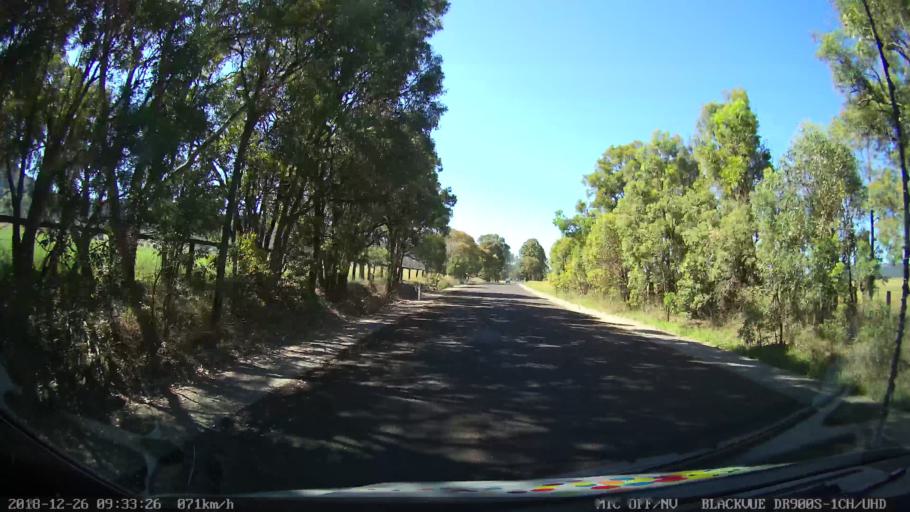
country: AU
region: New South Wales
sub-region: Mid-Western Regional
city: Kandos
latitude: -32.8947
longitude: 150.0350
